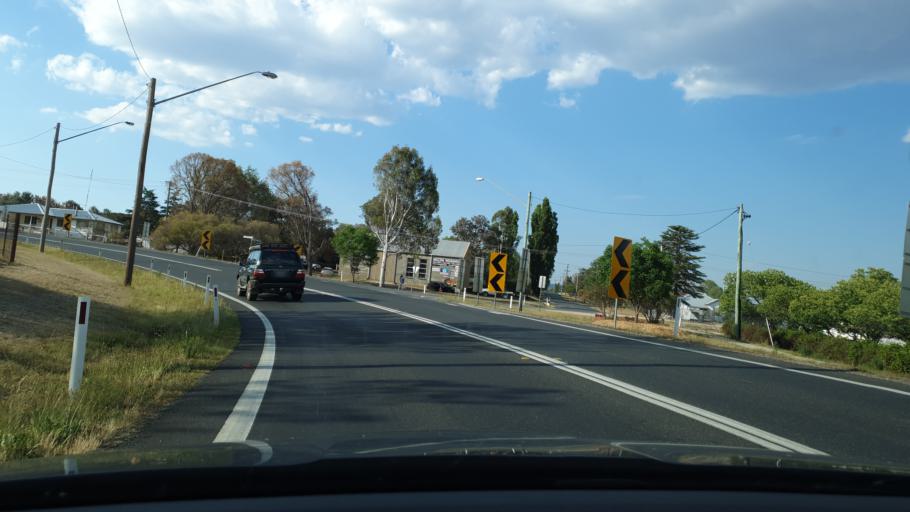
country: AU
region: New South Wales
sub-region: Tenterfield Municipality
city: Carrolls Creek
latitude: -29.0416
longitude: 152.0213
